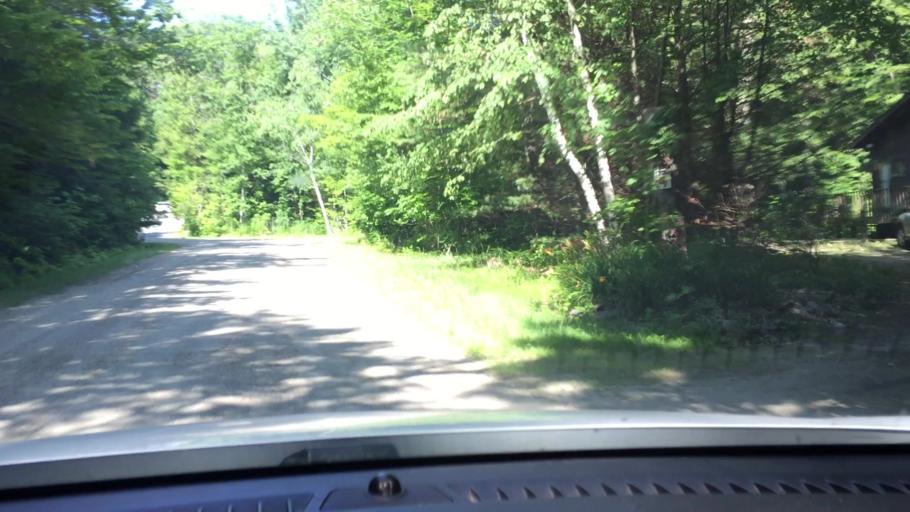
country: US
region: Massachusetts
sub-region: Berkshire County
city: Otis
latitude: 42.1839
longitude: -73.1031
